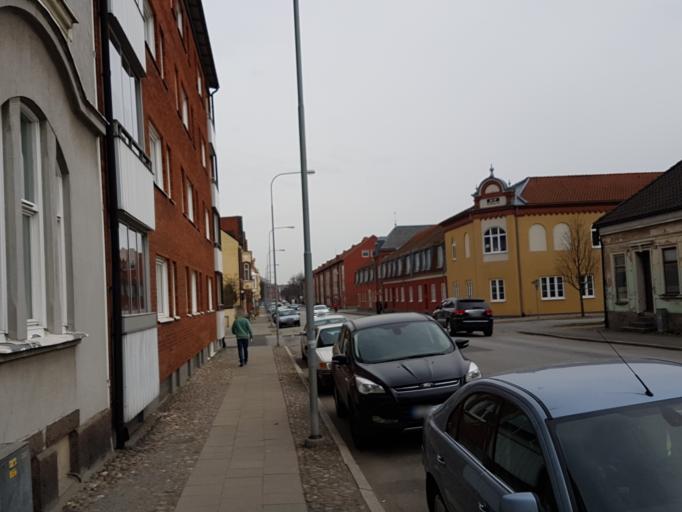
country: SE
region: Skane
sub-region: Ystads Kommun
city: Ystad
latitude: 55.4311
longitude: 13.8308
